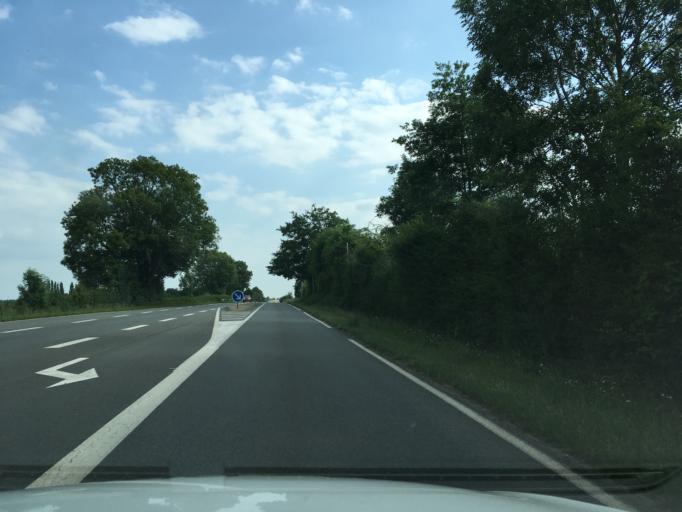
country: FR
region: Poitou-Charentes
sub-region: Departement des Deux-Sevres
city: Le Tallud
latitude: 46.5993
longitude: -0.2887
